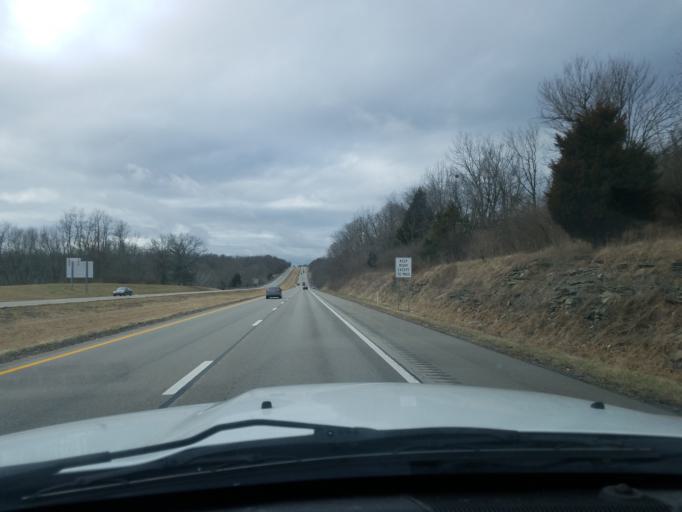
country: US
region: Kentucky
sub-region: Montgomery County
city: Mount Sterling
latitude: 38.0748
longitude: -83.9659
